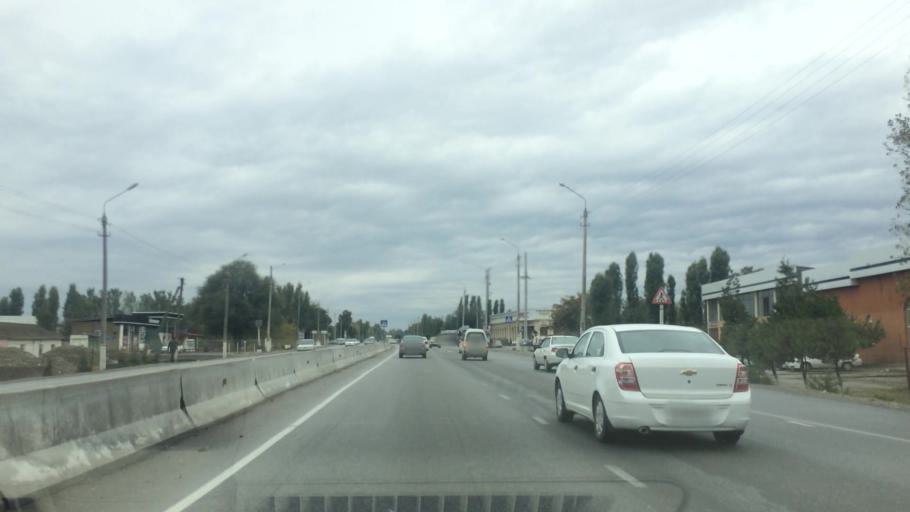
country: UZ
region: Jizzax
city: Jizzax
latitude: 40.0031
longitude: 67.5934
